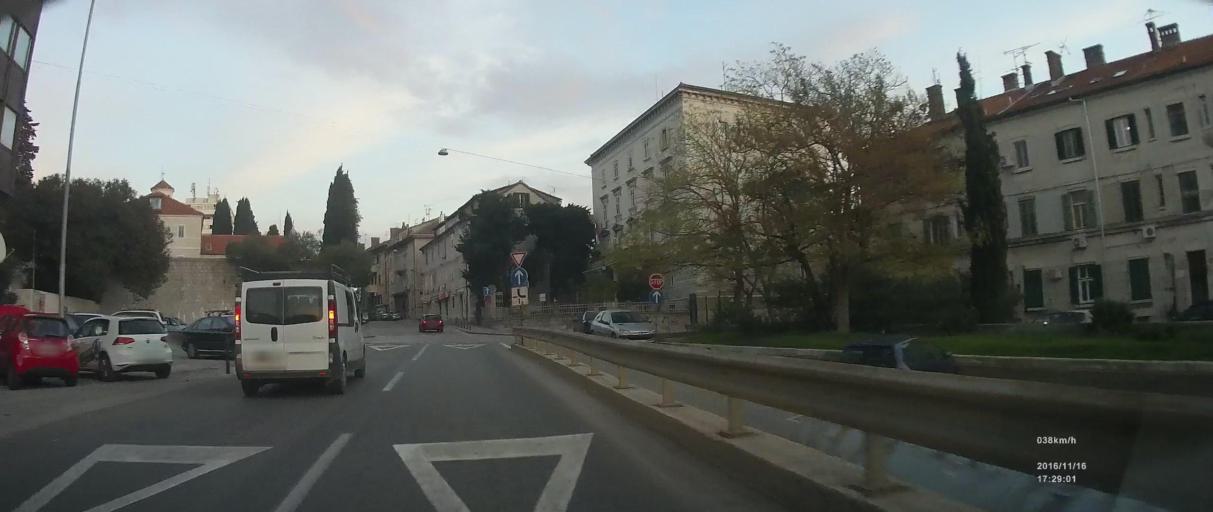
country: HR
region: Splitsko-Dalmatinska
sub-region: Grad Split
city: Split
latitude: 43.5059
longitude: 16.4455
